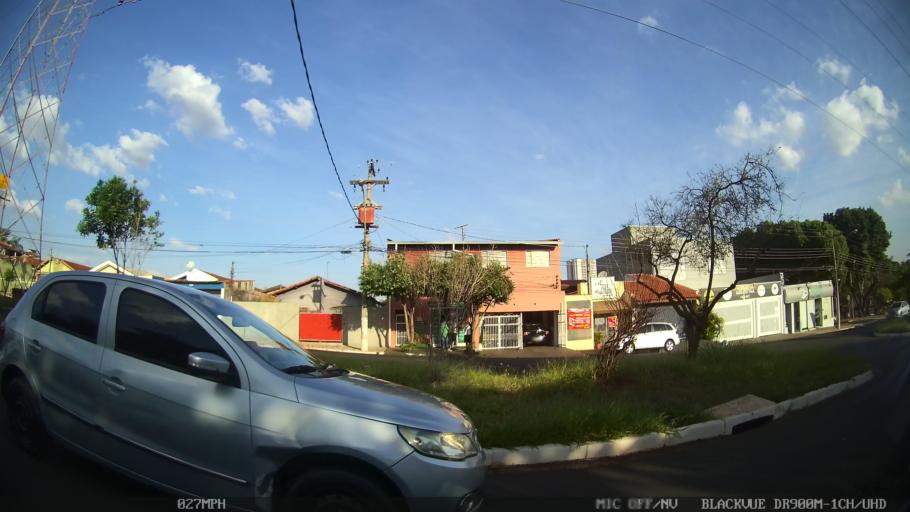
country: BR
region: Sao Paulo
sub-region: Ribeirao Preto
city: Ribeirao Preto
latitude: -21.1878
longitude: -47.7870
